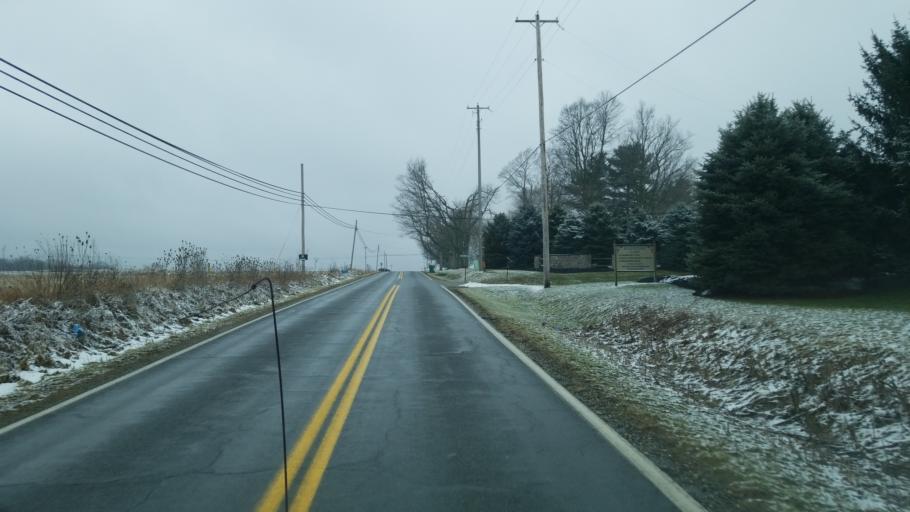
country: US
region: Ohio
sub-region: Portage County
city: Mantua
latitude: 41.2840
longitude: -81.2599
